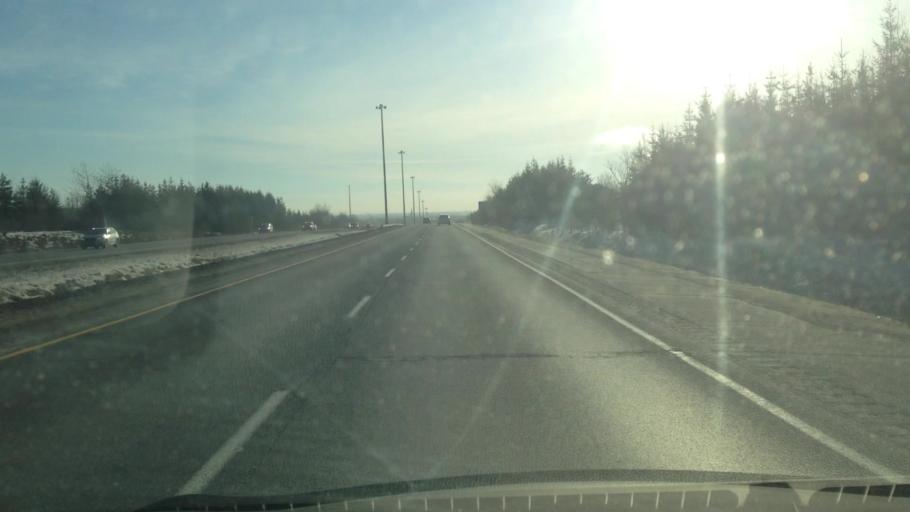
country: CA
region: Quebec
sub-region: Laurentides
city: Saint-Jerome
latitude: 45.8061
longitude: -74.0378
